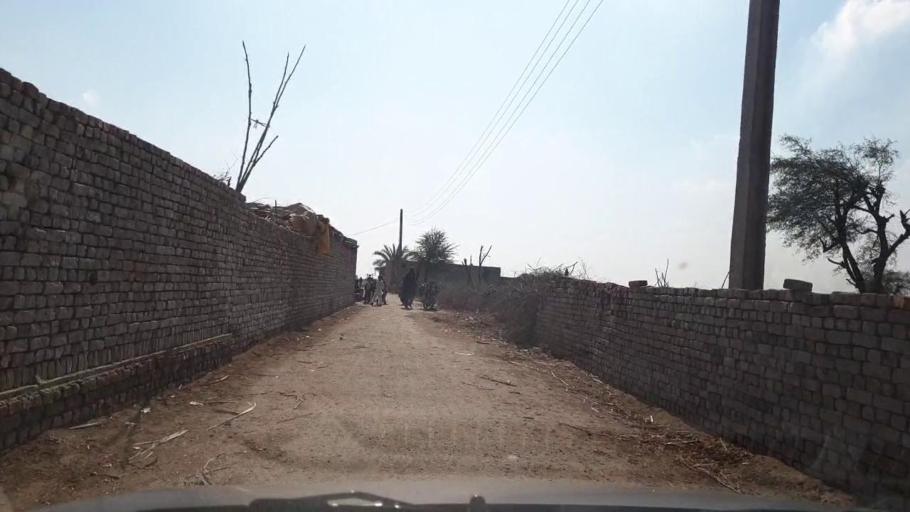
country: PK
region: Sindh
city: Khadro
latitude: 26.0785
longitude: 68.7445
